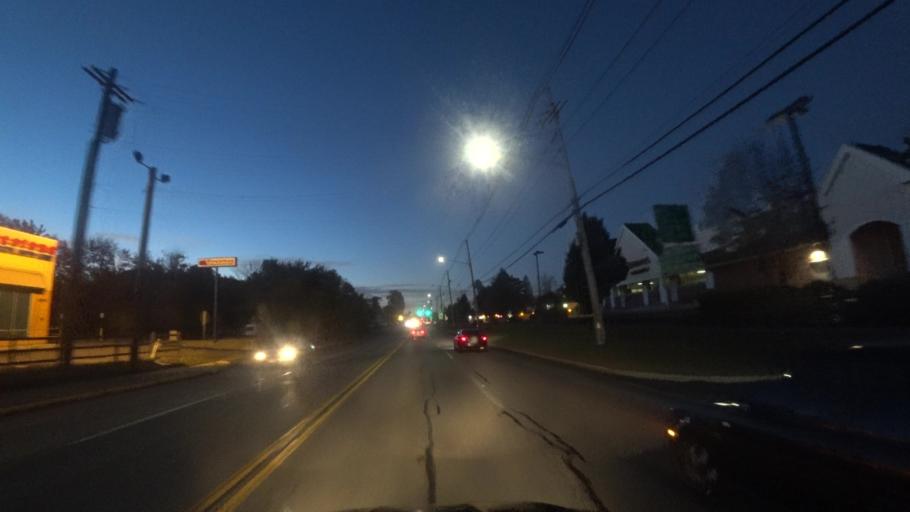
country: US
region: Massachusetts
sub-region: Middlesex County
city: North Reading
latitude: 42.5822
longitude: -71.1128
